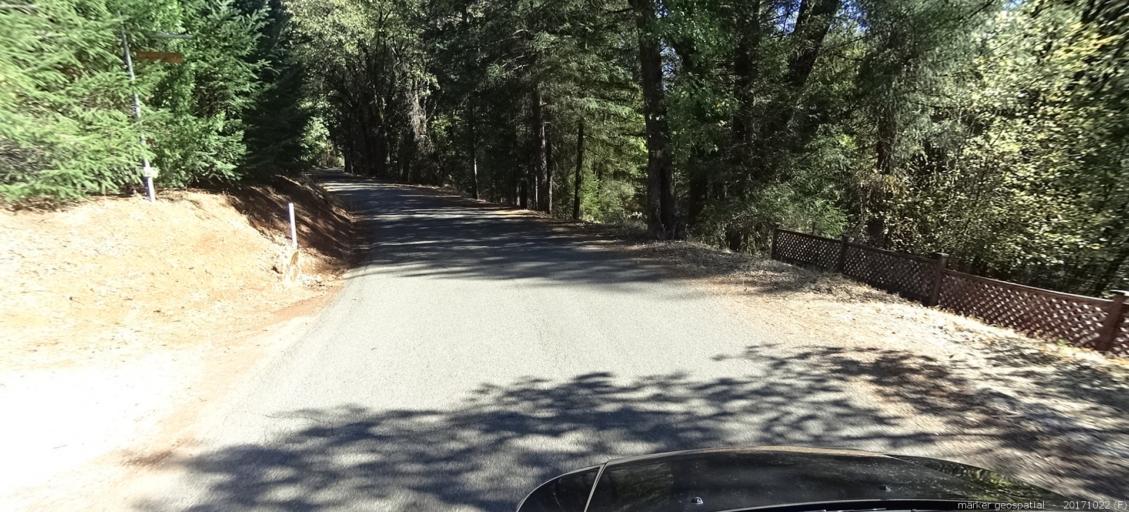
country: US
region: California
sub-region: Shasta County
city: Central Valley (historical)
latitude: 40.9394
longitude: -122.4482
